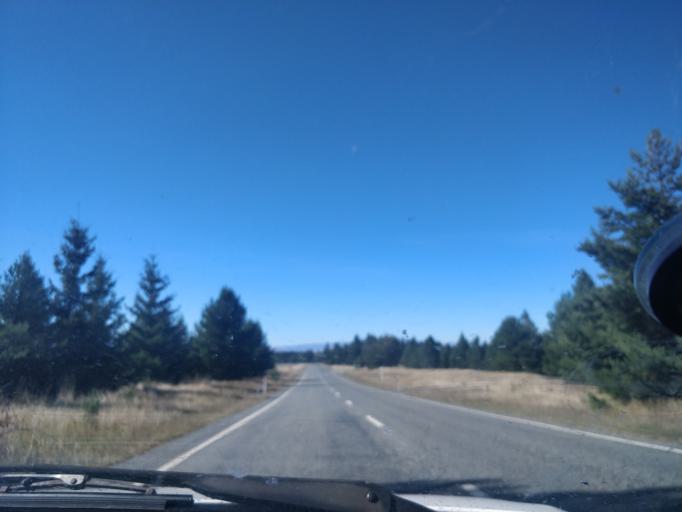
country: NZ
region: Otago
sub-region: Queenstown-Lakes District
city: Wanaka
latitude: -44.2721
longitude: 170.0499
